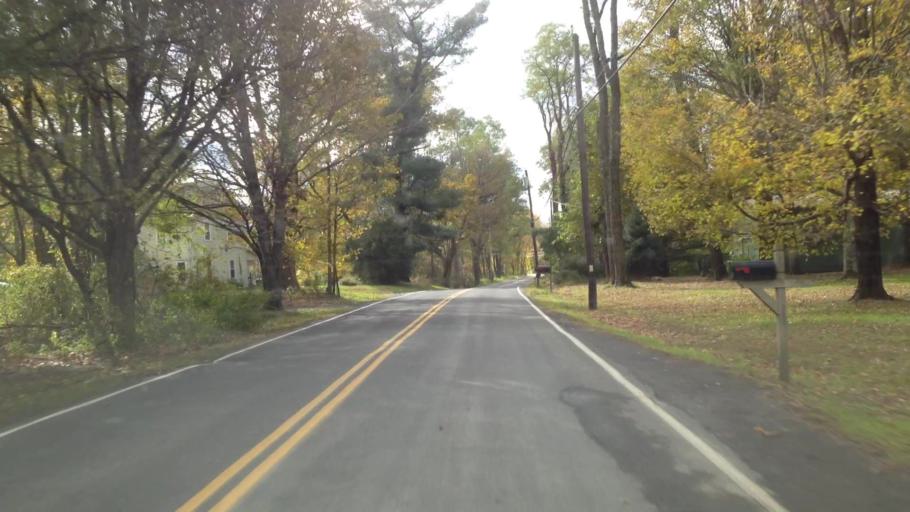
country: US
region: New York
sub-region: Ulster County
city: Tillson
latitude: 41.7959
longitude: -74.0871
